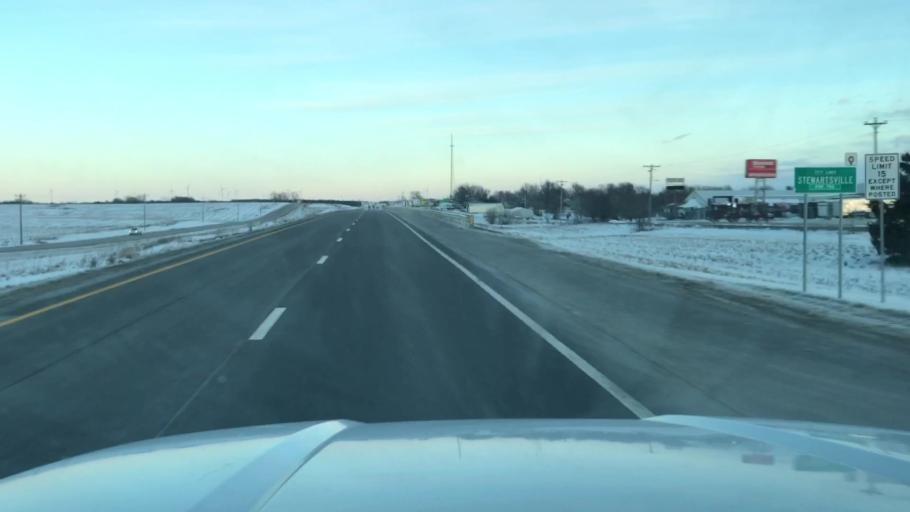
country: US
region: Missouri
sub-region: Clinton County
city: Gower
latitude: 39.7620
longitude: -94.5078
